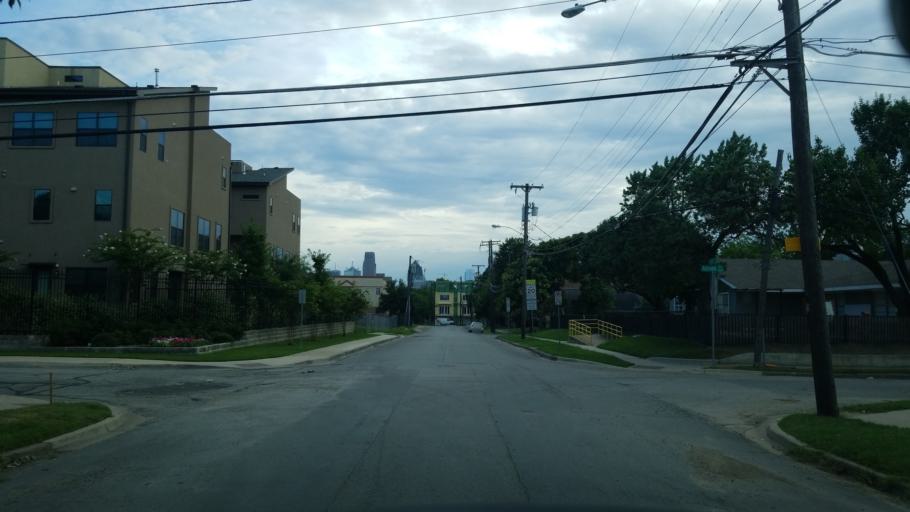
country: US
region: Texas
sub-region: Dallas County
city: Highland Park
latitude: 32.8052
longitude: -96.7803
